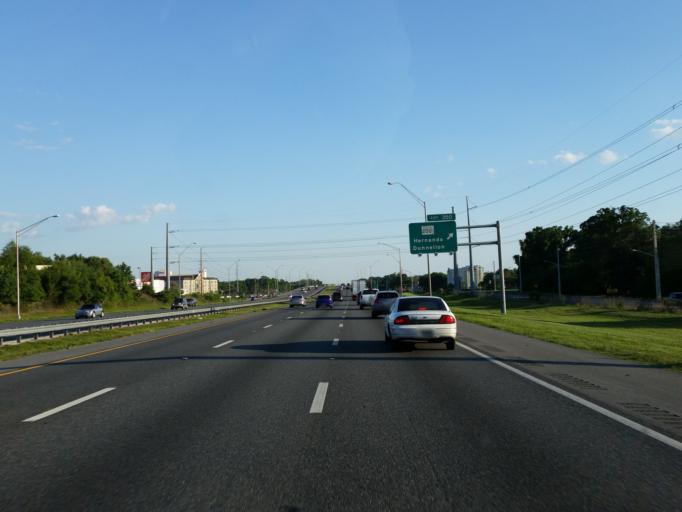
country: US
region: Florida
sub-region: Marion County
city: Ocala
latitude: 29.1565
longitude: -82.1852
